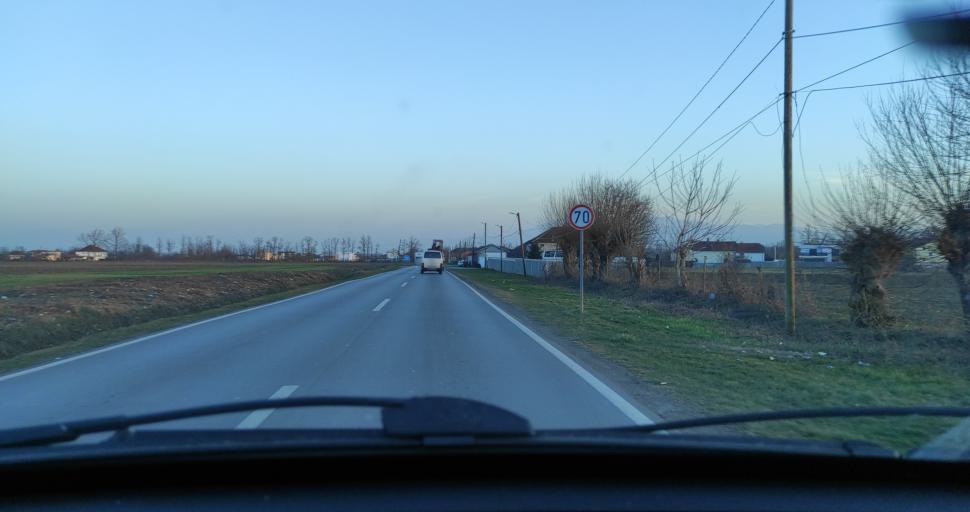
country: XK
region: Gjakova
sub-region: Komuna e Gjakoves
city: Gjakove
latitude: 42.4245
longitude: 20.3902
